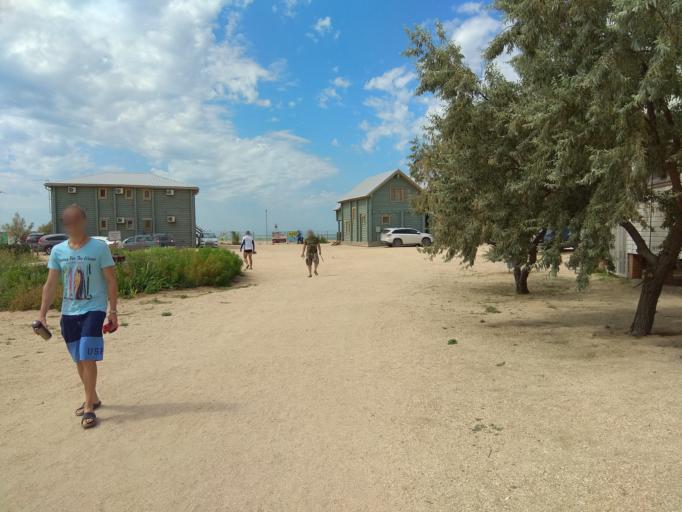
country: RU
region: Krasnodarskiy
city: Dolzhanskaya
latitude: 46.6803
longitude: 37.7383
